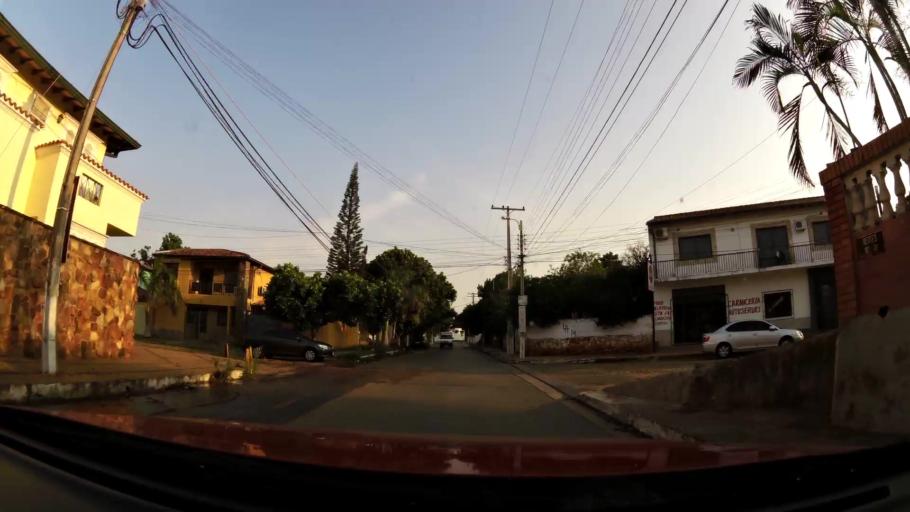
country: PY
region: Central
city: Lambare
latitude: -25.3495
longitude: -57.6059
